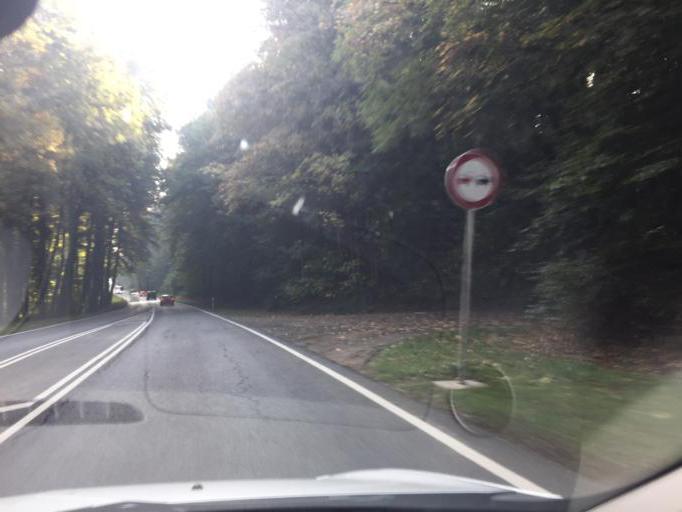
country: LU
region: Luxembourg
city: Schrassig
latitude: 49.5999
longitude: 6.2426
